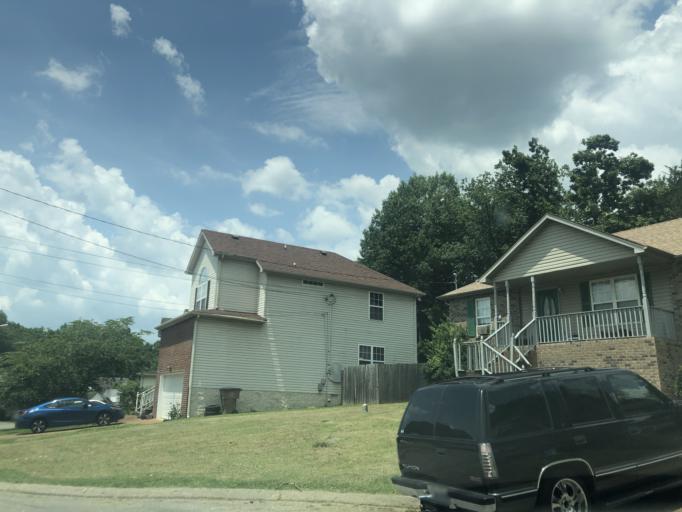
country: US
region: Tennessee
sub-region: Rutherford County
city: La Vergne
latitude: 36.0561
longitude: -86.6544
